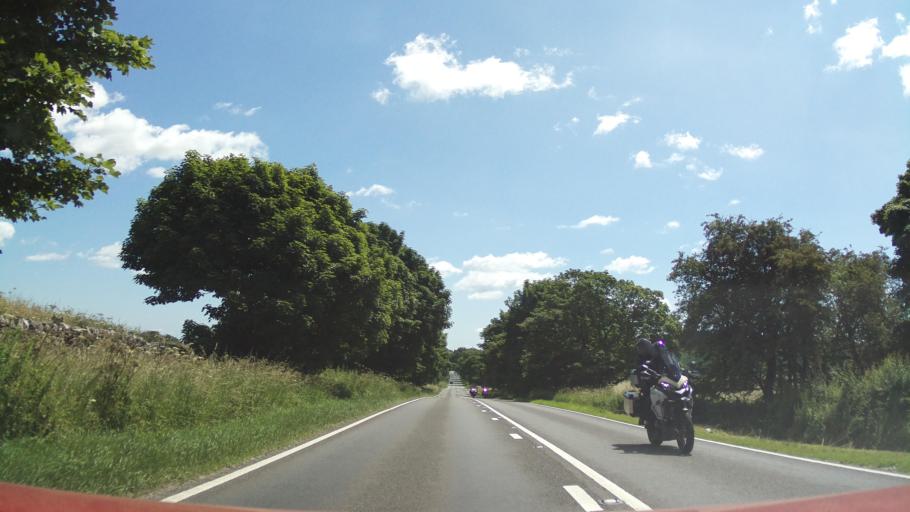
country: GB
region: England
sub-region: Derbyshire
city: Bakewell
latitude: 53.1472
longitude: -1.7642
